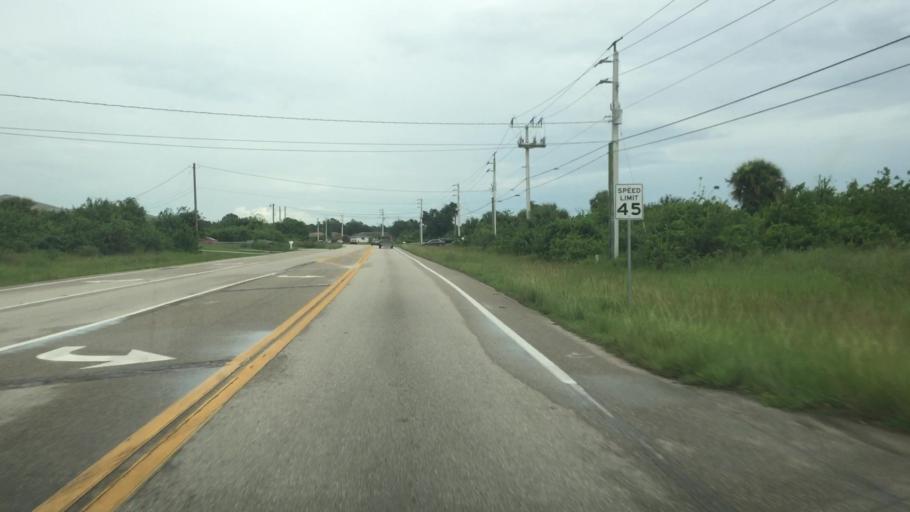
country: US
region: Florida
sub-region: Lee County
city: Gateway
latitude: 26.5998
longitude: -81.7340
